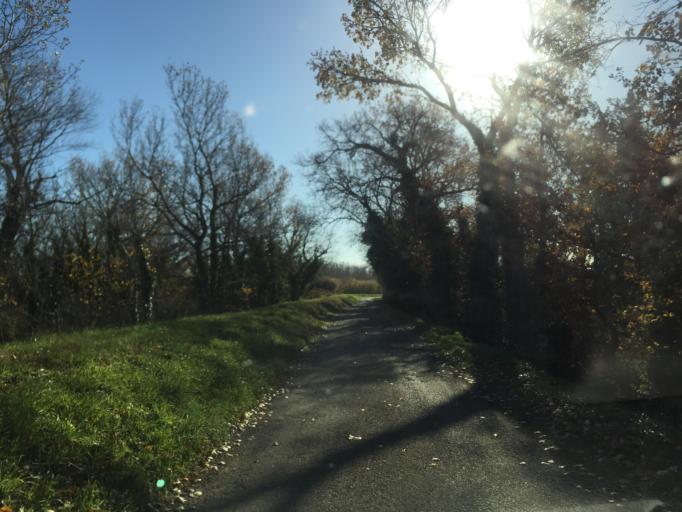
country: FR
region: Provence-Alpes-Cote d'Azur
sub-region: Departement du Vaucluse
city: Sarrians
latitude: 44.0713
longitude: 4.9293
